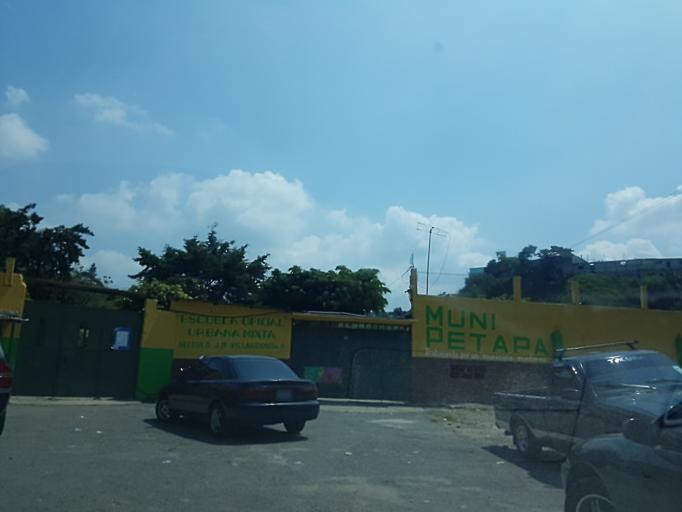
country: GT
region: Guatemala
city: Petapa
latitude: 14.5281
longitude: -90.5494
